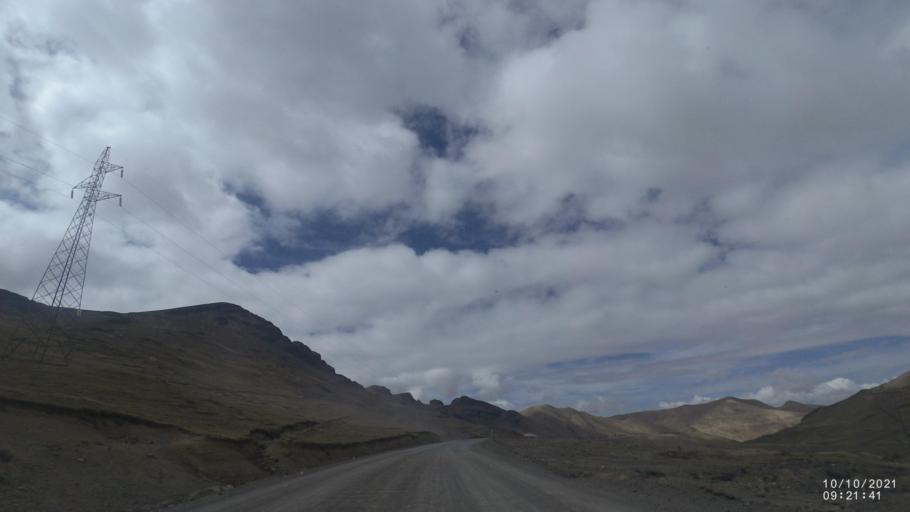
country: BO
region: La Paz
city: Quime
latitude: -17.0701
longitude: -67.2987
